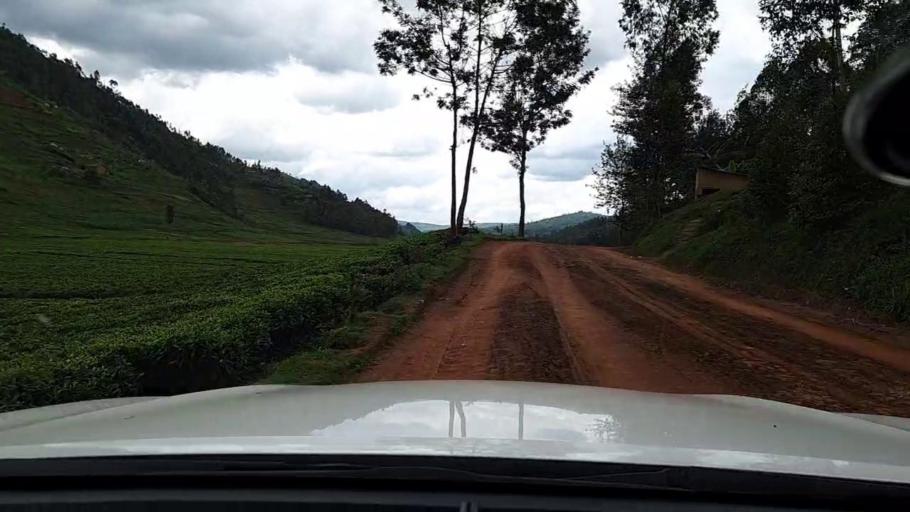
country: RW
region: Northern Province
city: Byumba
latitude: -1.6651
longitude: 29.9189
